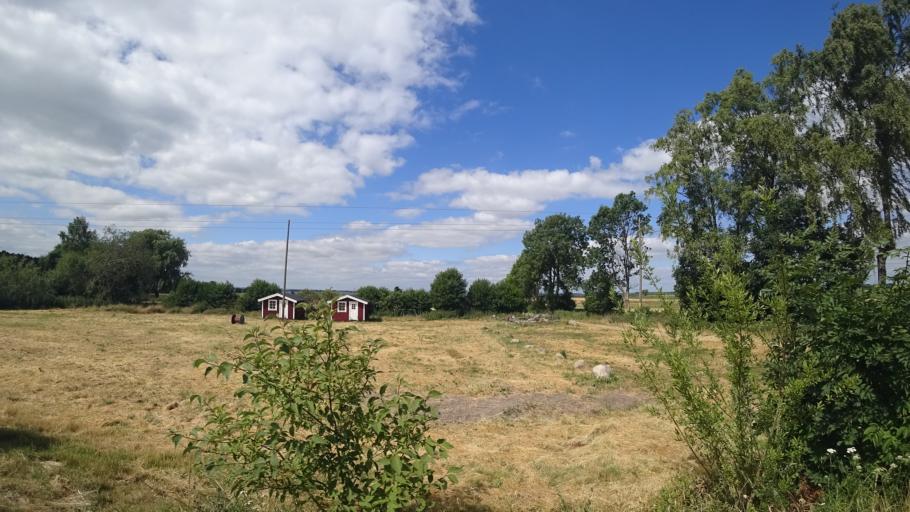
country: SE
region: Skane
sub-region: Kristianstads Kommun
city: Ahus
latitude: 55.9777
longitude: 14.2649
